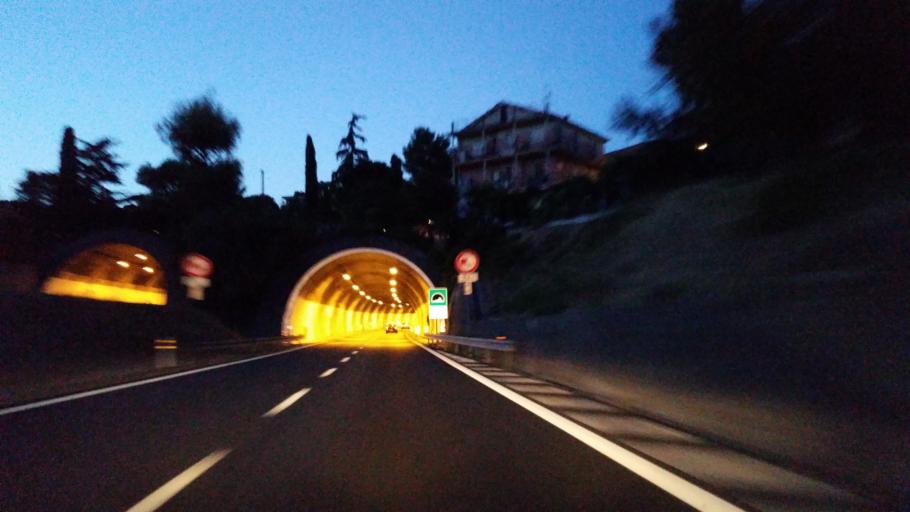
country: IT
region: Liguria
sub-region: Provincia di Imperia
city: Diano Castello
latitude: 43.9170
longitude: 8.0698
